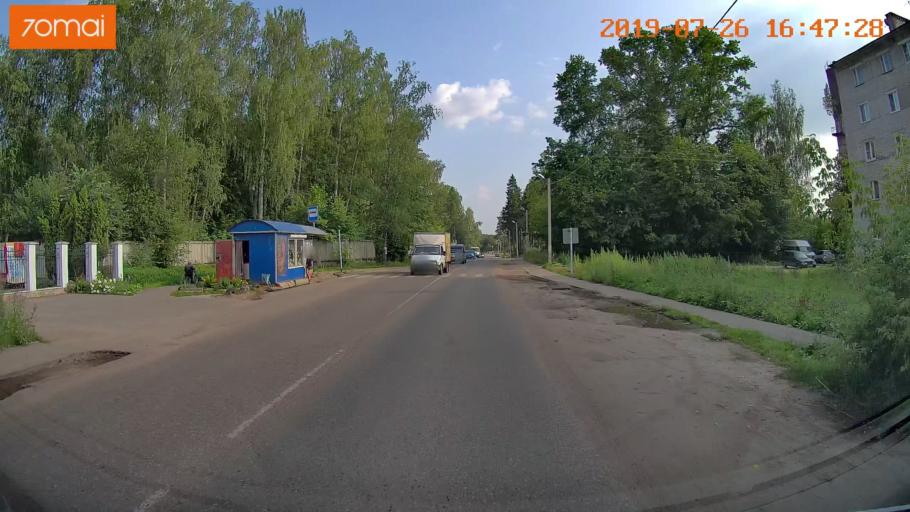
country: RU
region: Ivanovo
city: Bogorodskoye
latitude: 57.0411
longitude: 41.0121
